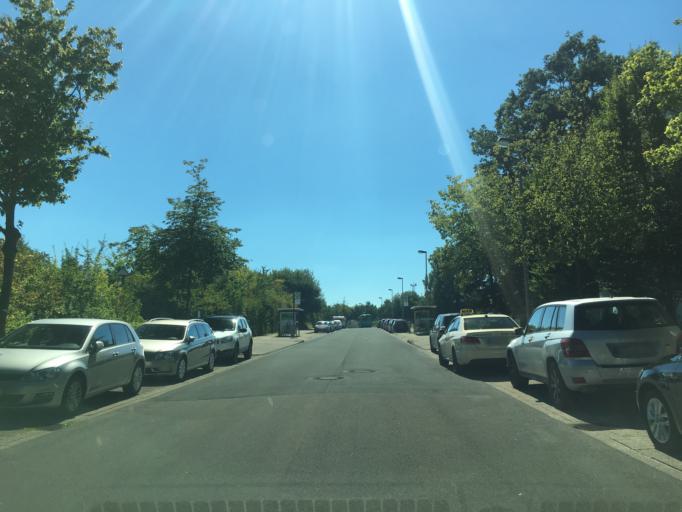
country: DE
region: North Rhine-Westphalia
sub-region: Regierungsbezirk Munster
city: Muenster
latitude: 51.9914
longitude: 7.6173
